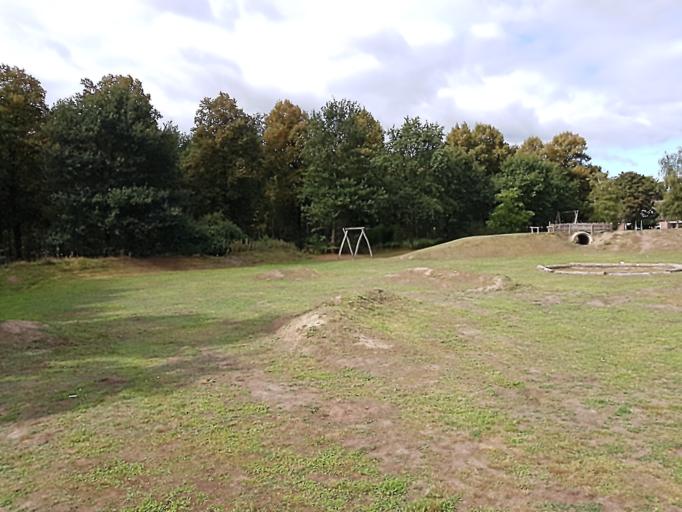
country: NL
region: North Brabant
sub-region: Gemeente Best
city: Best
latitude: 51.4904
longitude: 5.3984
